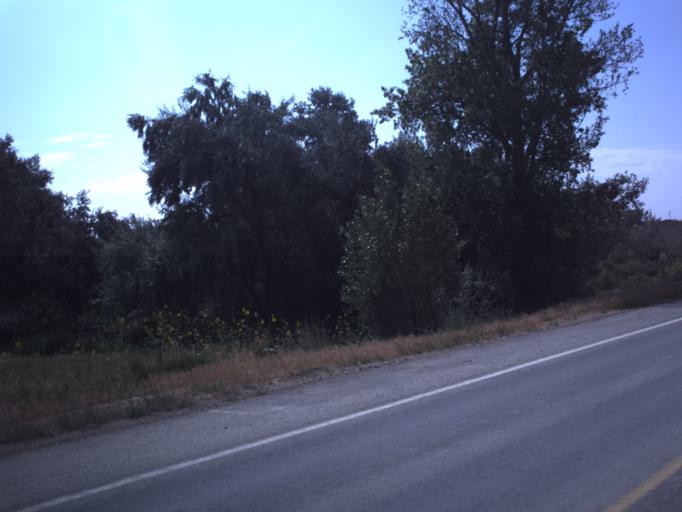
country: US
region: Utah
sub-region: Uintah County
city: Naples
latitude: 40.3744
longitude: -109.4984
